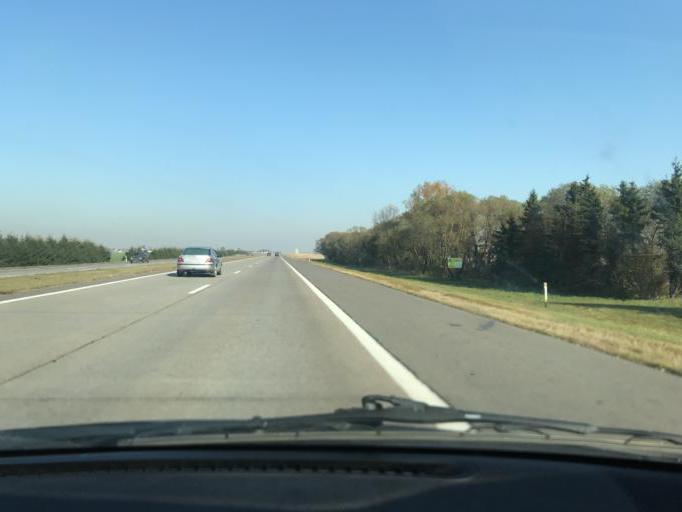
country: BY
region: Minsk
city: Samakhvalavichy
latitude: 53.6625
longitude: 27.4839
